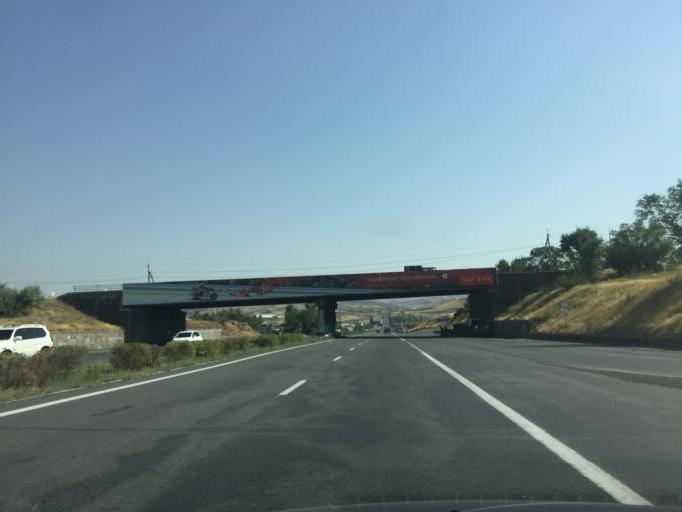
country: AM
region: Kotayk'i Marz
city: Arzni
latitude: 40.2845
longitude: 44.6059
